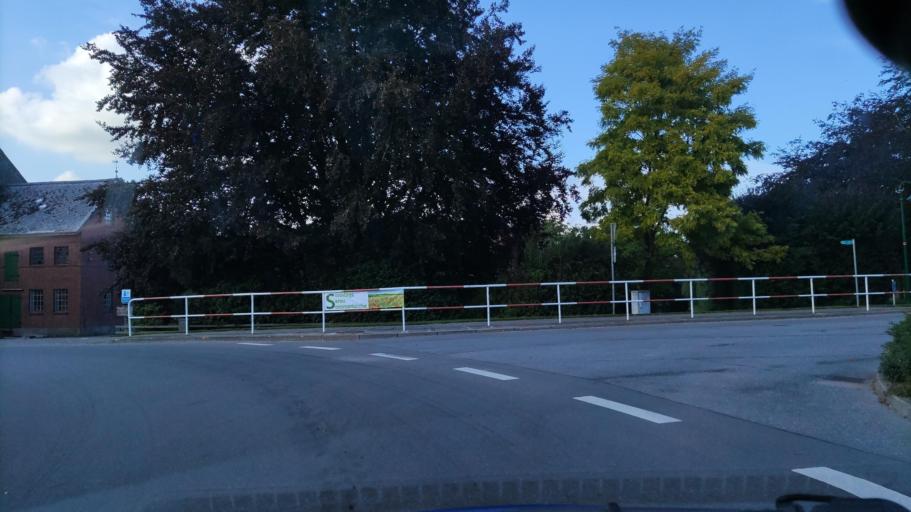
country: DE
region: Schleswig-Holstein
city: Glasau
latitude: 54.0577
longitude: 10.5318
